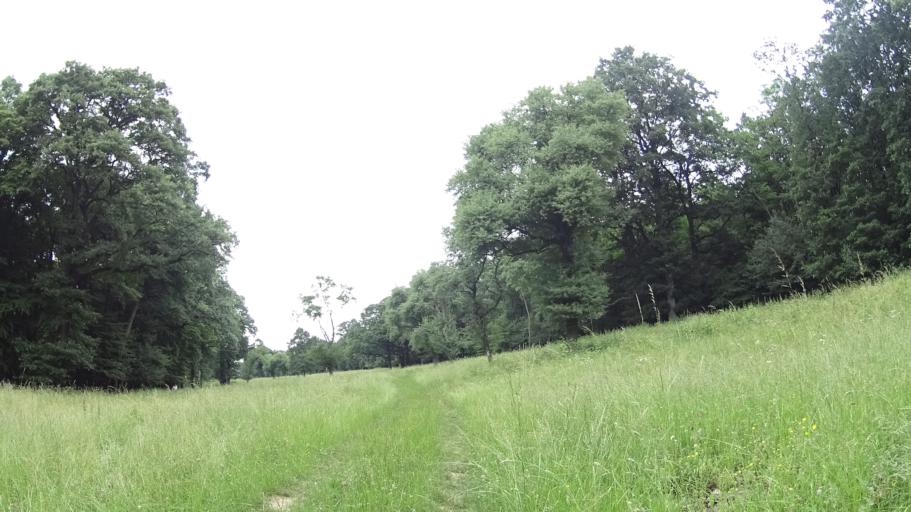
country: HU
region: Pest
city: Nagymaros
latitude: 47.8084
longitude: 18.9404
